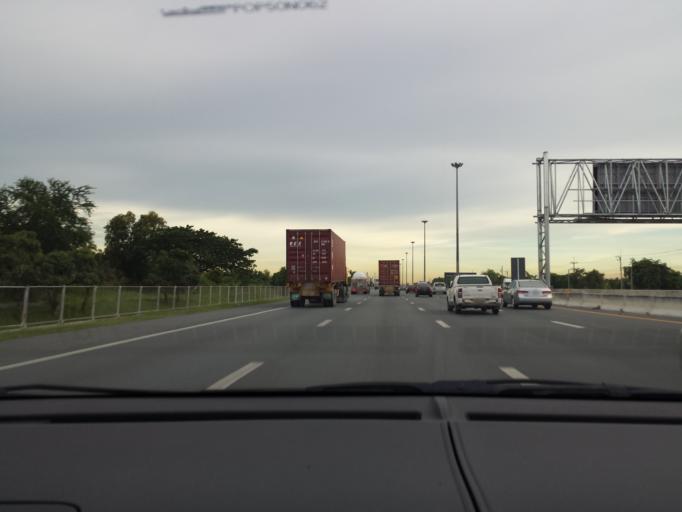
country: TH
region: Pathum Thani
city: Thanyaburi
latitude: 14.0374
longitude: 100.6983
